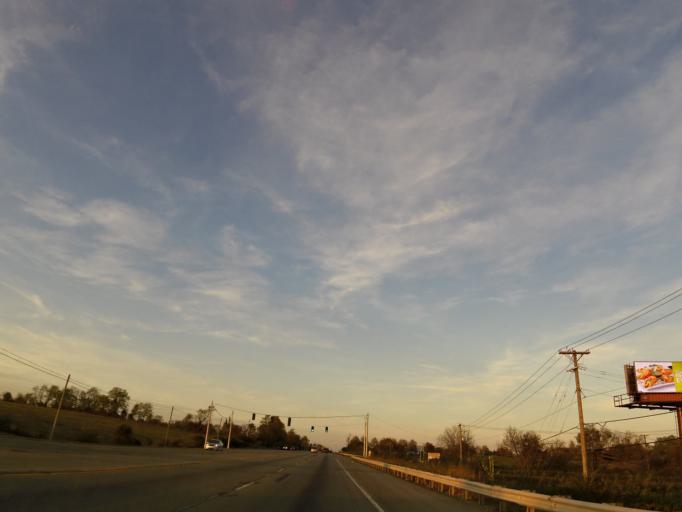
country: US
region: Kentucky
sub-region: Fayette County
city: Monticello
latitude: 37.9406
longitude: -84.5466
